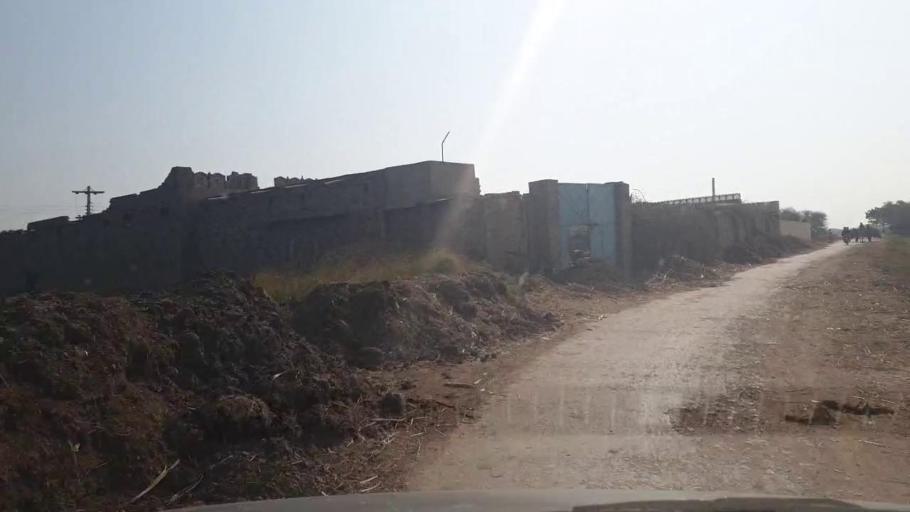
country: PK
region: Sindh
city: Tando Adam
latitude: 25.7450
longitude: 68.6165
